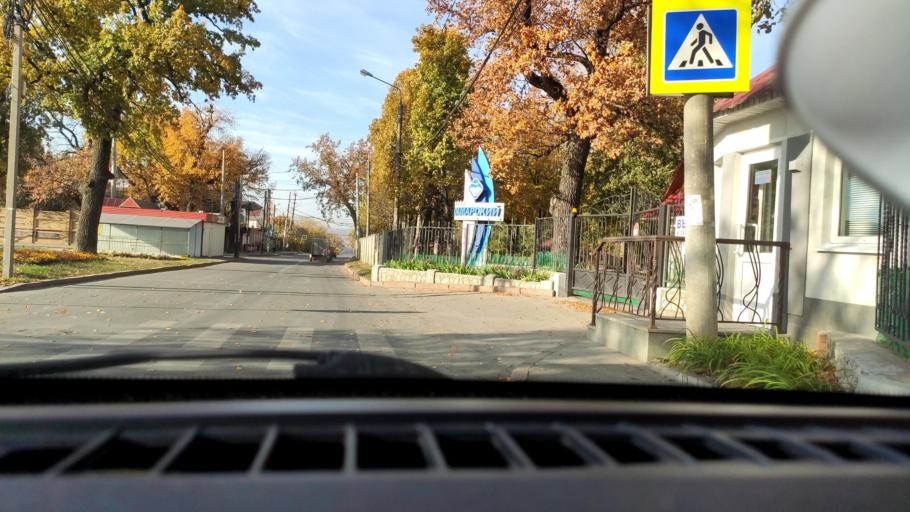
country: RU
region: Samara
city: Samara
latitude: 53.2752
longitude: 50.1918
